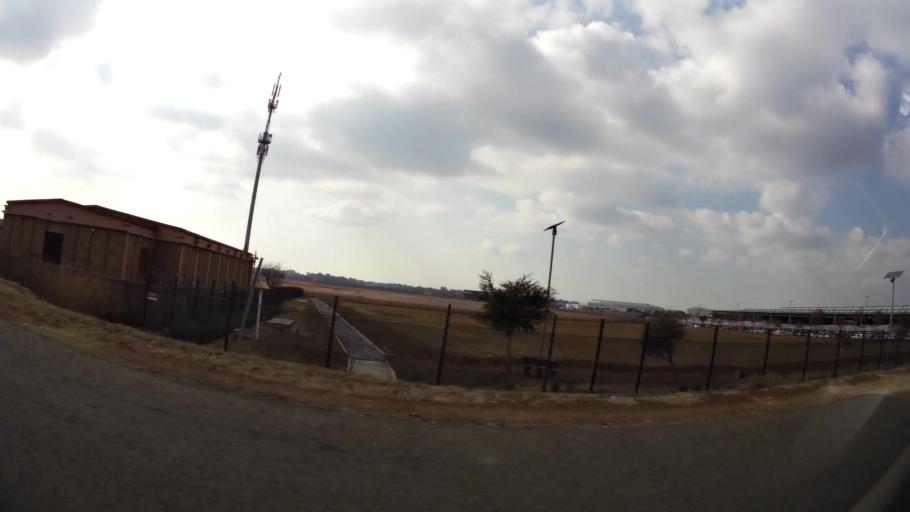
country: ZA
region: Gauteng
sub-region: Ekurhuleni Metropolitan Municipality
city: Benoni
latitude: -26.1362
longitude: 28.2688
